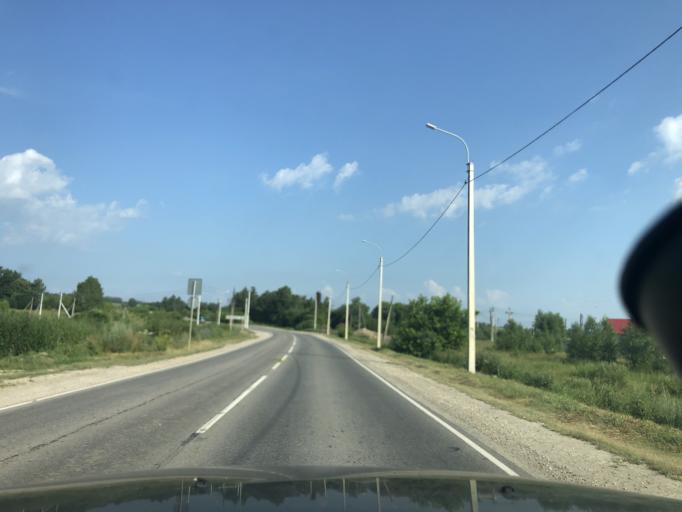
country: RU
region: Tula
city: Dubna
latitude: 54.1078
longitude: 37.1060
